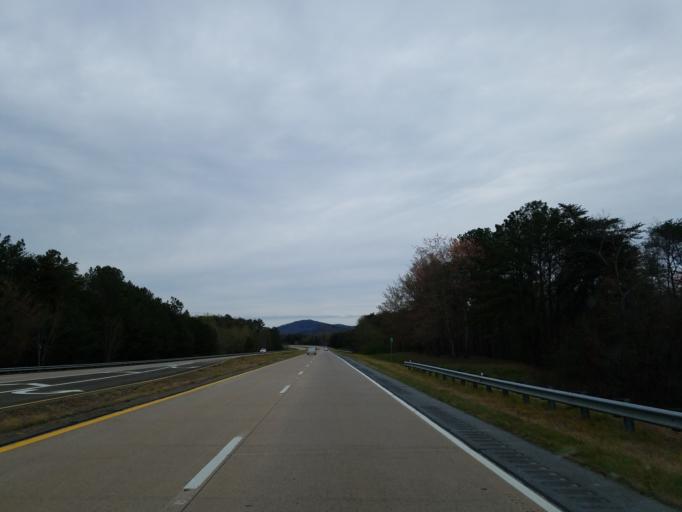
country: US
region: Georgia
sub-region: Gilmer County
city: Ellijay
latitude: 34.5790
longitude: -84.5197
